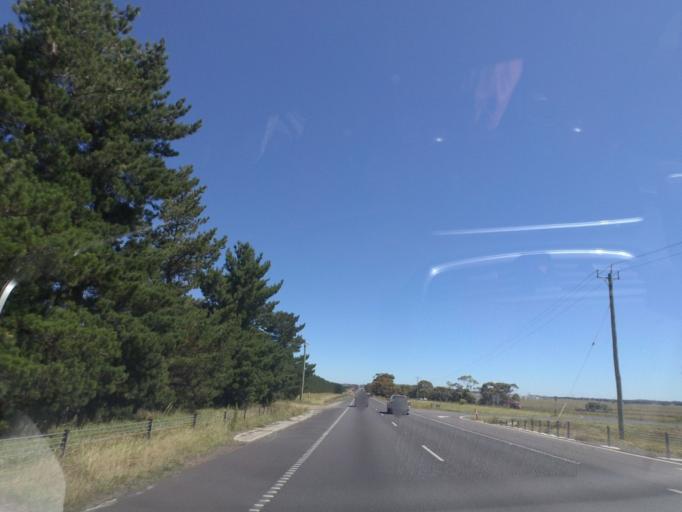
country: AU
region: Victoria
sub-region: Hume
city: Craigieburn
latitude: -37.5162
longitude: 144.9495
